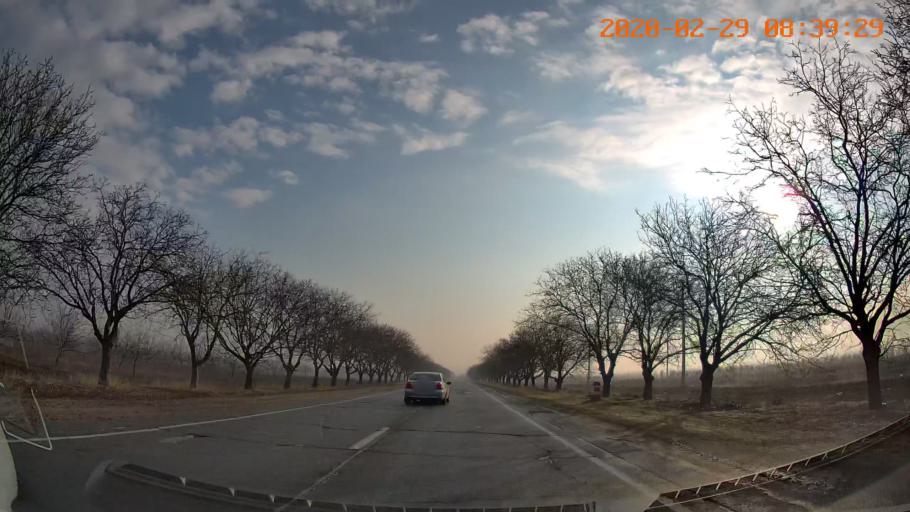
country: MD
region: Anenii Noi
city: Varnita
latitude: 46.9225
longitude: 29.3986
